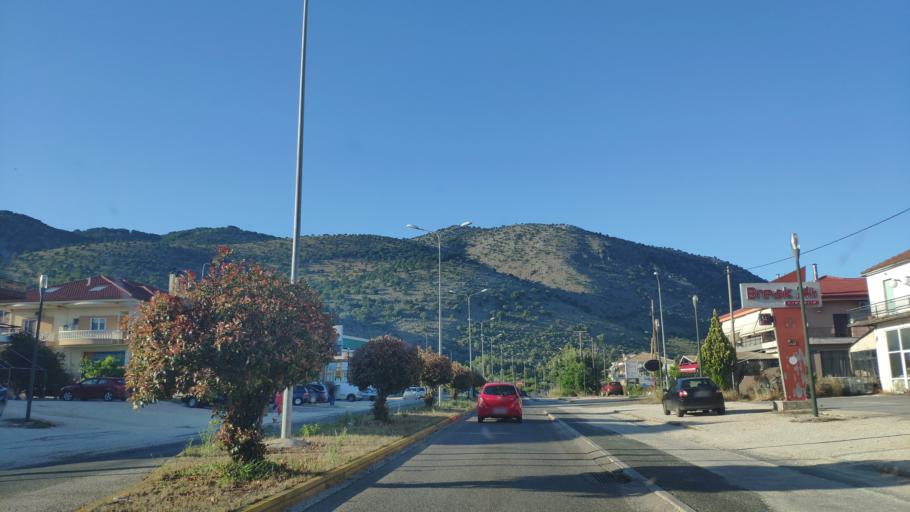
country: GR
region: Epirus
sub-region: Nomos Prevezis
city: Louros
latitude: 39.1694
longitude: 20.7600
